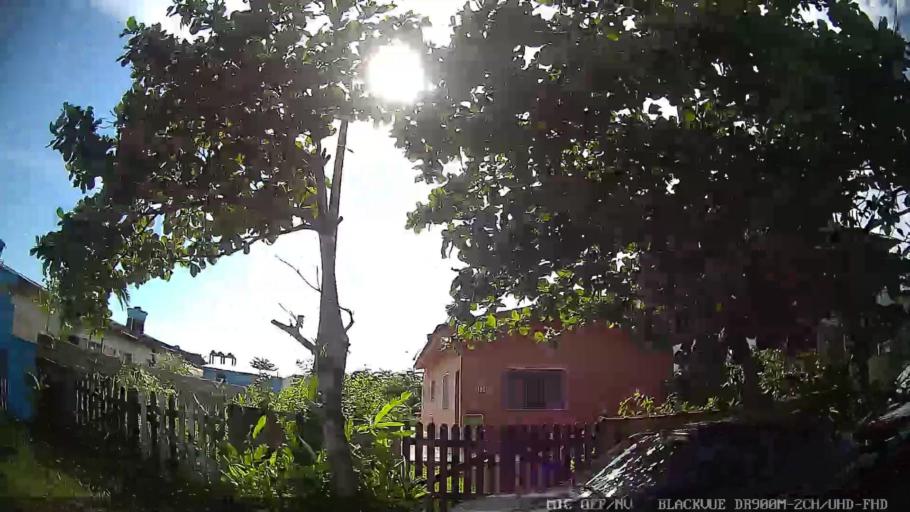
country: BR
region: Sao Paulo
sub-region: Iguape
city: Iguape
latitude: -24.7697
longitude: -47.5868
